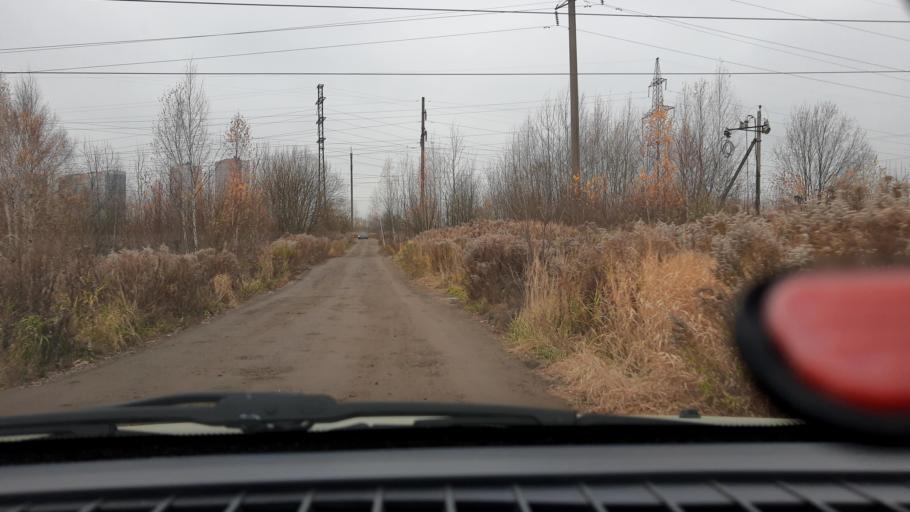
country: RU
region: Nizjnij Novgorod
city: Afonino
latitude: 56.2551
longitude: 44.0517
